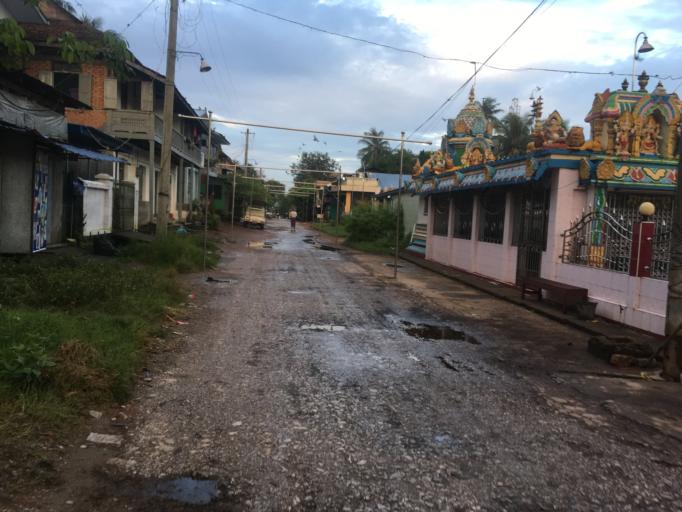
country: MM
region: Mon
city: Mawlamyine
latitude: 16.4642
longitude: 97.6280
